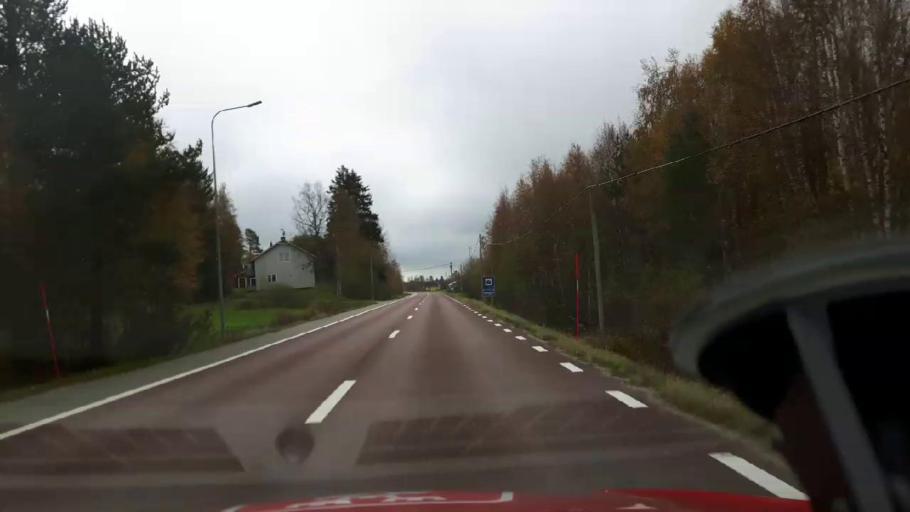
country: SE
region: Jaemtland
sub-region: Harjedalens Kommun
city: Sveg
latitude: 62.2891
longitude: 14.7943
